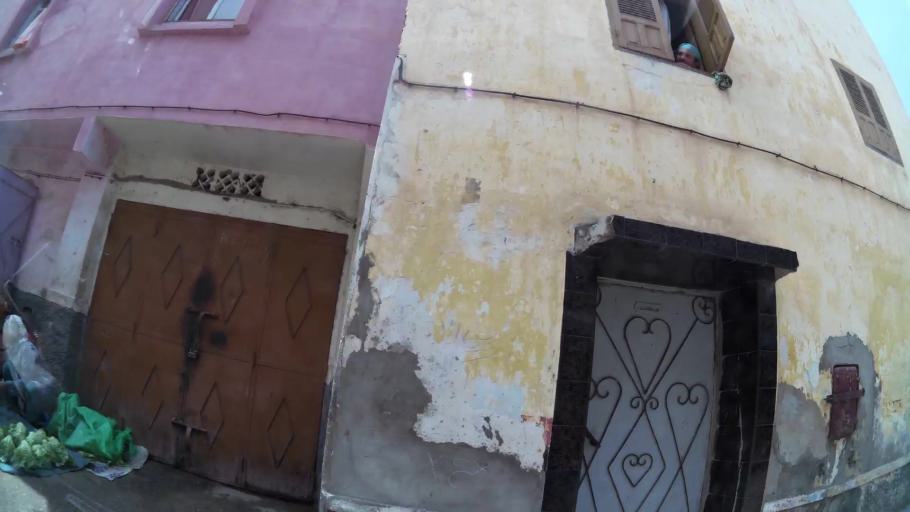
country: MA
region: Rabat-Sale-Zemmour-Zaer
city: Sale
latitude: 34.0524
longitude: -6.7884
